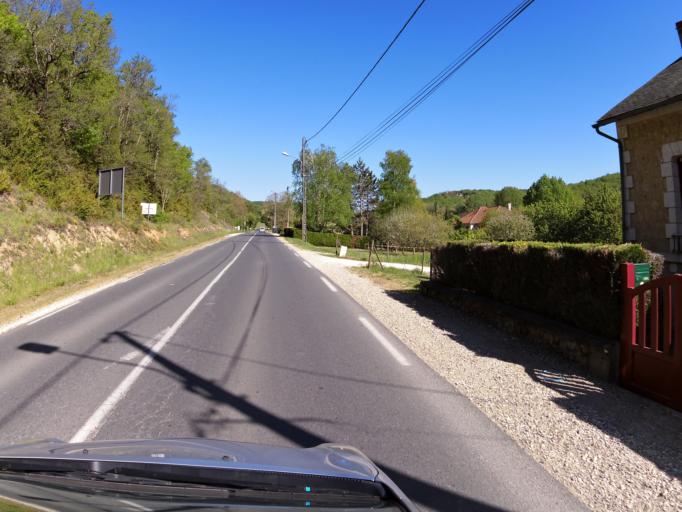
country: FR
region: Aquitaine
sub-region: Departement de la Dordogne
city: Montignac
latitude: 45.0638
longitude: 1.1782
